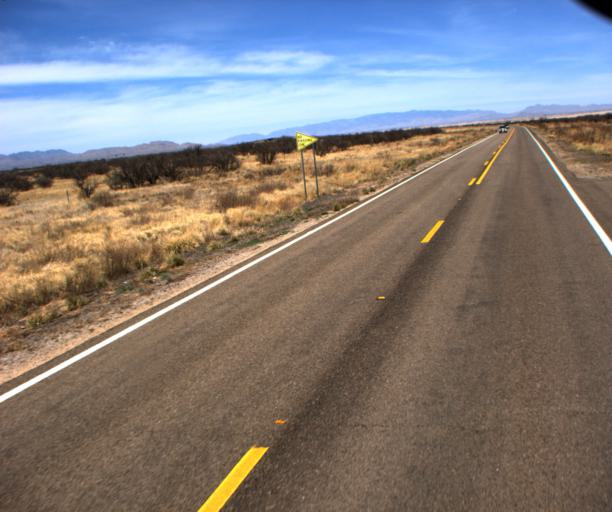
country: US
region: Arizona
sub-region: Cochise County
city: Willcox
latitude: 32.1240
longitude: -109.9093
